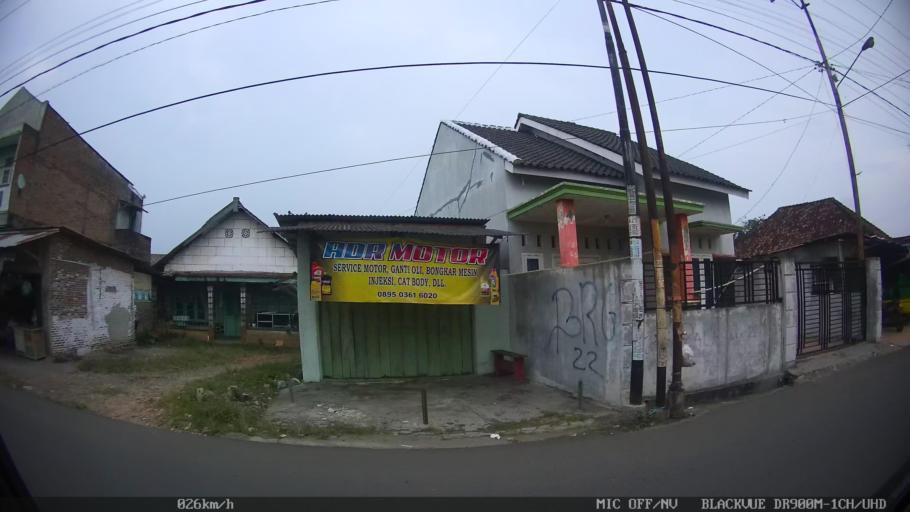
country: ID
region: Lampung
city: Bandarlampung
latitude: -5.4049
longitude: 105.2654
